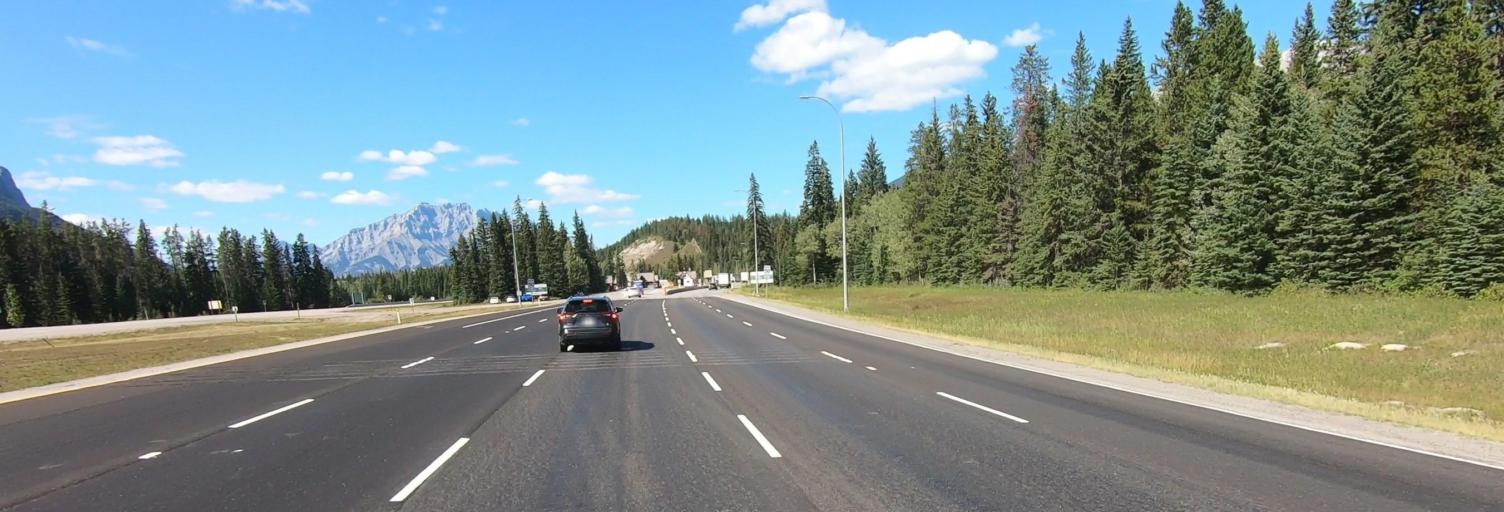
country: CA
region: Alberta
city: Canmore
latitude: 51.1326
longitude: -115.4037
